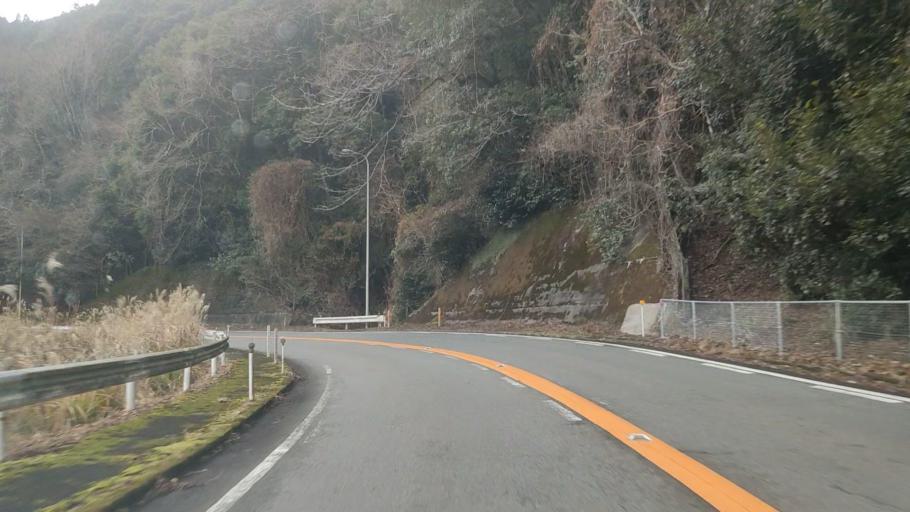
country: JP
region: Kumamoto
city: Hitoyoshi
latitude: 32.1218
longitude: 130.8076
